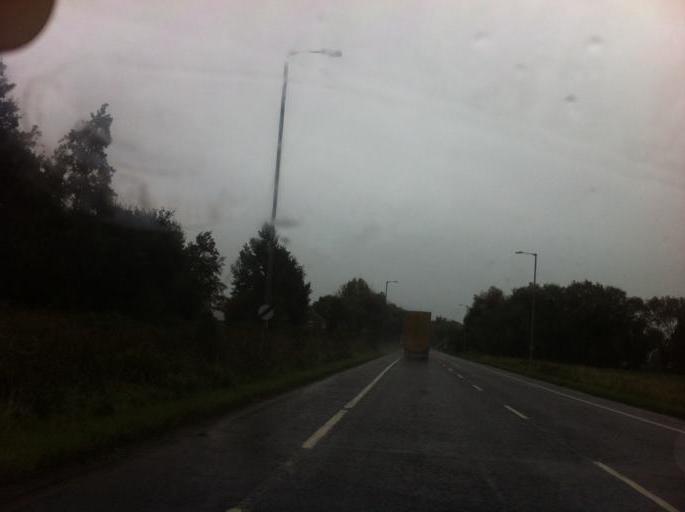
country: GB
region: England
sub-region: Lincolnshire
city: Kirton
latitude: 52.9292
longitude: -0.0521
